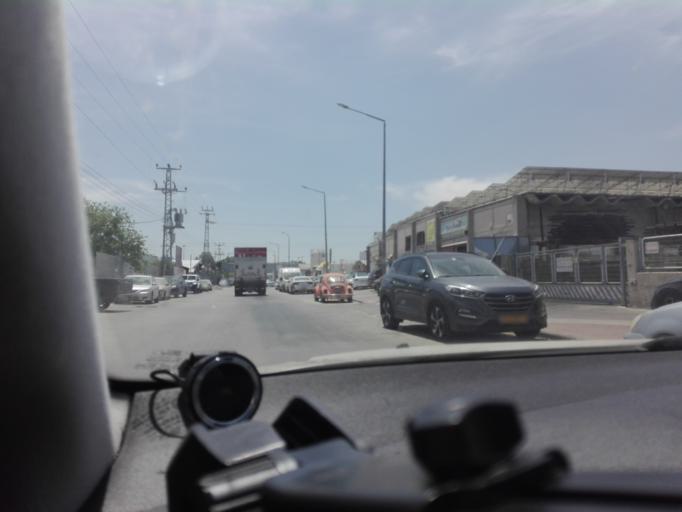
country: IL
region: Central District
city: Bene 'Ayish
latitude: 31.7358
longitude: 34.7541
